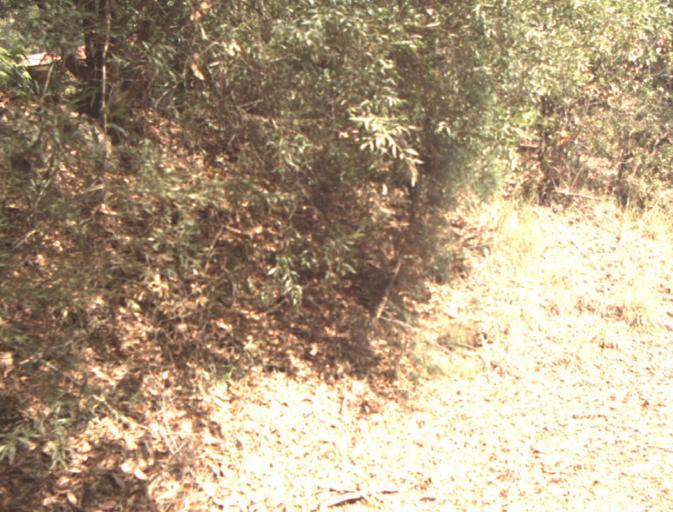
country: AU
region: Tasmania
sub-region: Launceston
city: Mayfield
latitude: -41.2572
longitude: 147.1874
